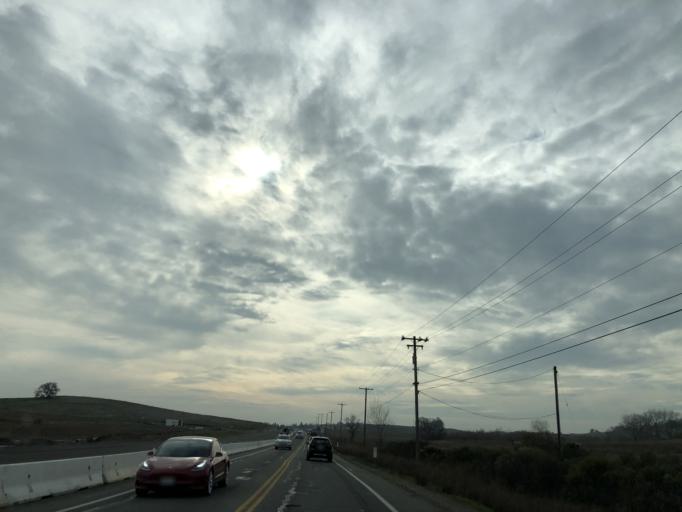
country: US
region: California
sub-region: El Dorado County
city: El Dorado Hills
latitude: 38.6982
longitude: -121.1163
